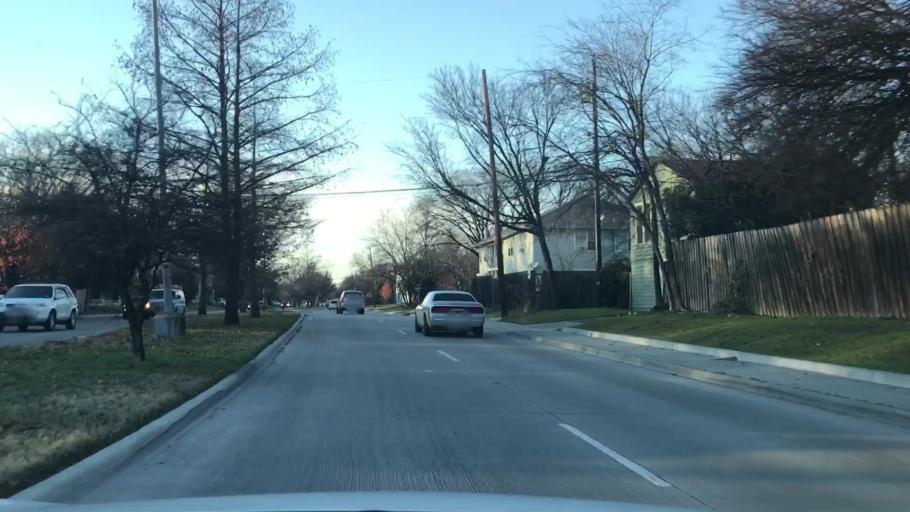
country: US
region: Texas
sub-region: Dallas County
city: Highland Park
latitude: 32.7993
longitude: -96.7616
